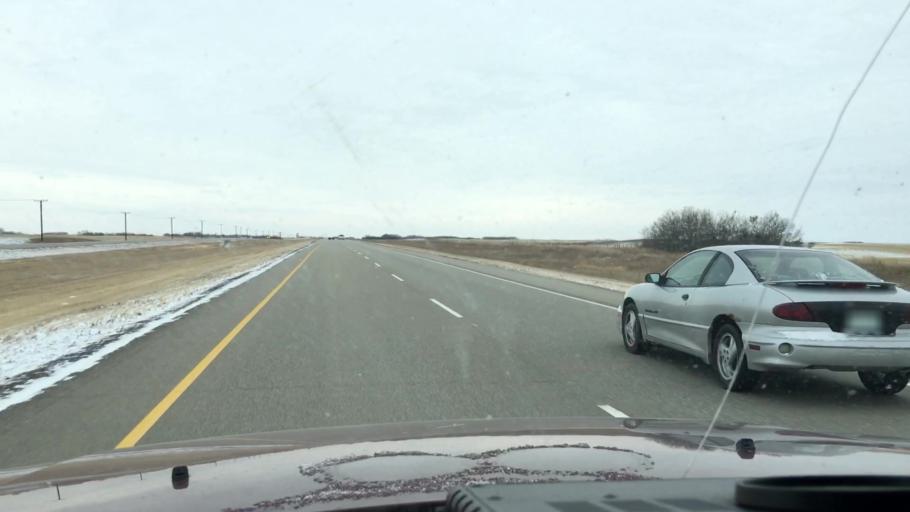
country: CA
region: Saskatchewan
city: Watrous
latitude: 51.4047
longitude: -106.1804
